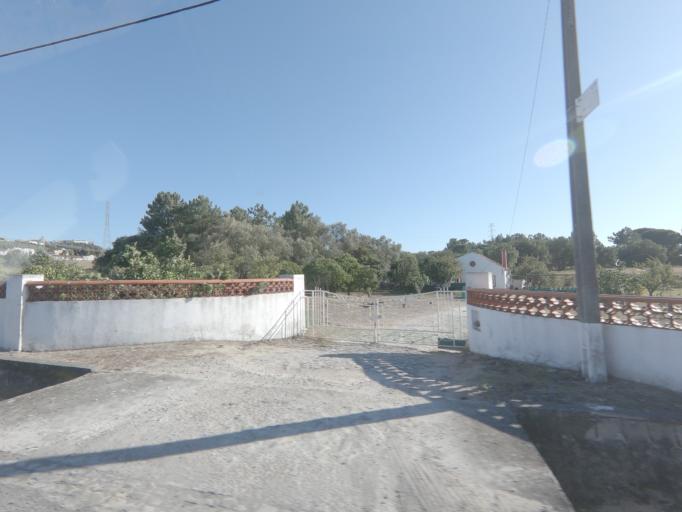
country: PT
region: Setubal
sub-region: Palmela
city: Palmela
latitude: 38.5822
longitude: -8.9108
